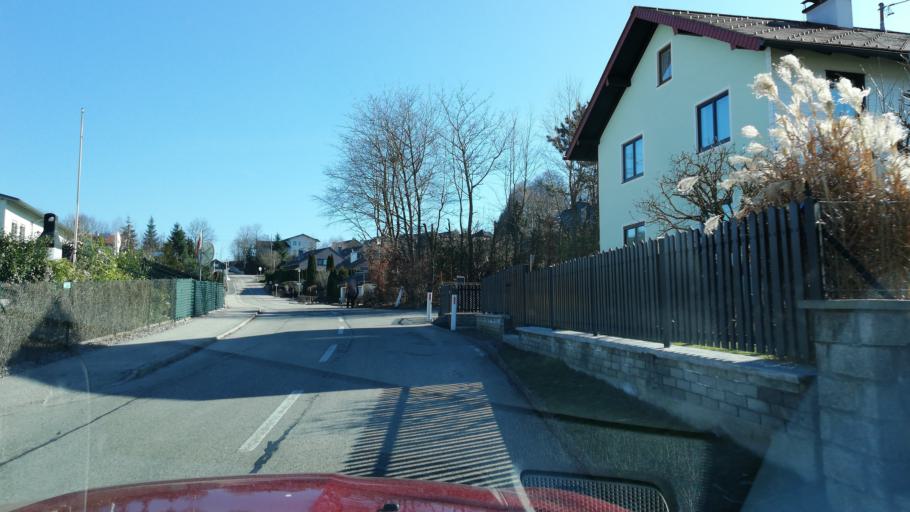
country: AT
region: Upper Austria
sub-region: Politischer Bezirk Vocklabruck
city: Lenzing
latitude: 47.9621
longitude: 13.6102
